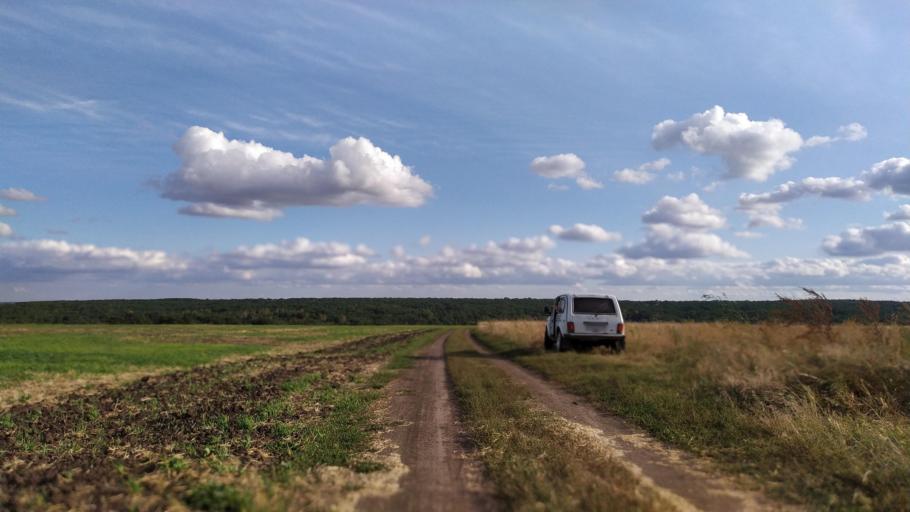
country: RU
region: Kursk
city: Kursk
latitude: 51.6113
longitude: 36.1663
